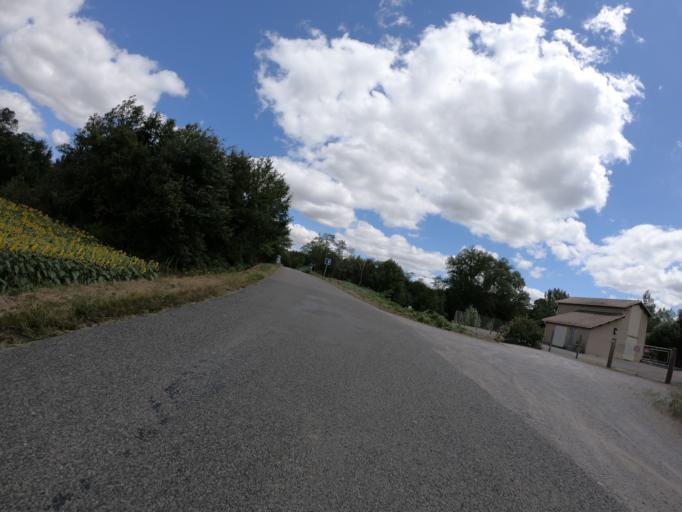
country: FR
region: Midi-Pyrenees
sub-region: Departement de l'Ariege
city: La Tour-du-Crieu
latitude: 43.0974
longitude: 1.7446
